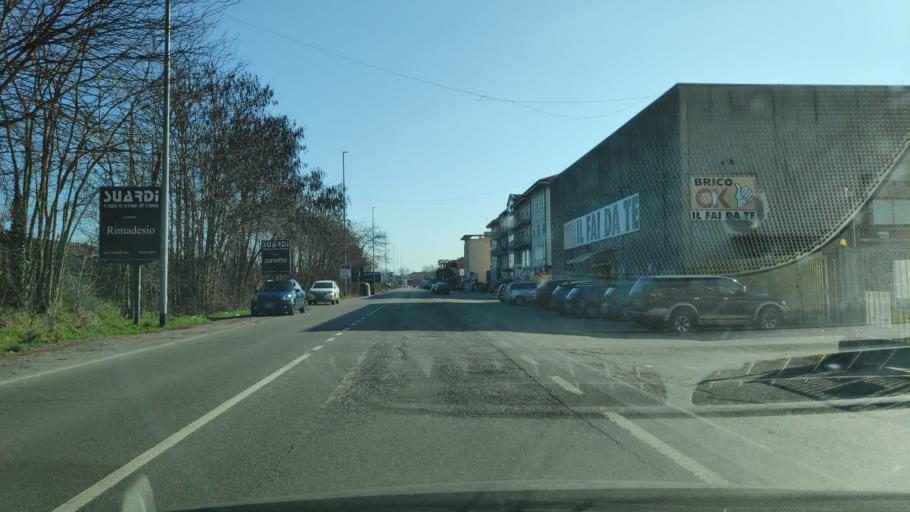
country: IT
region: Lombardy
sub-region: Provincia di Pavia
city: Pavia
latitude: 45.2031
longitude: 9.1494
